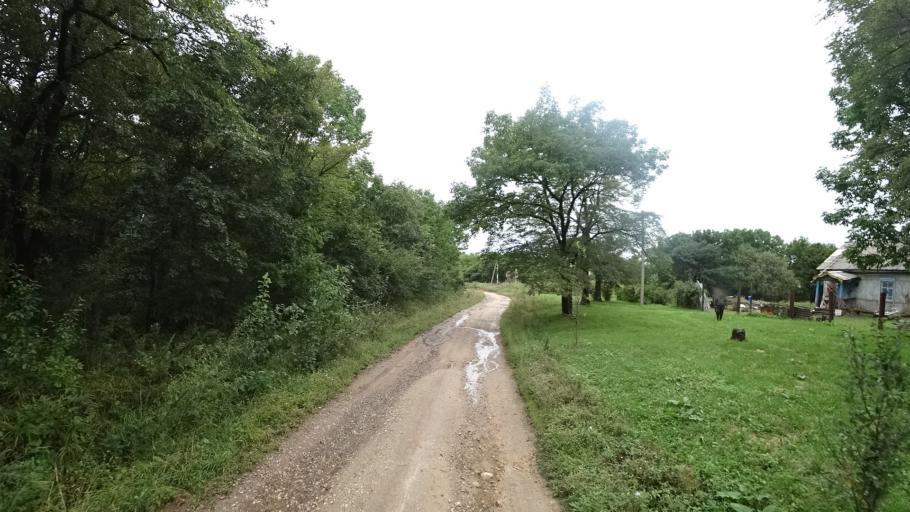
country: RU
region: Primorskiy
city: Rettikhovka
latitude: 44.0564
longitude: 132.6658
